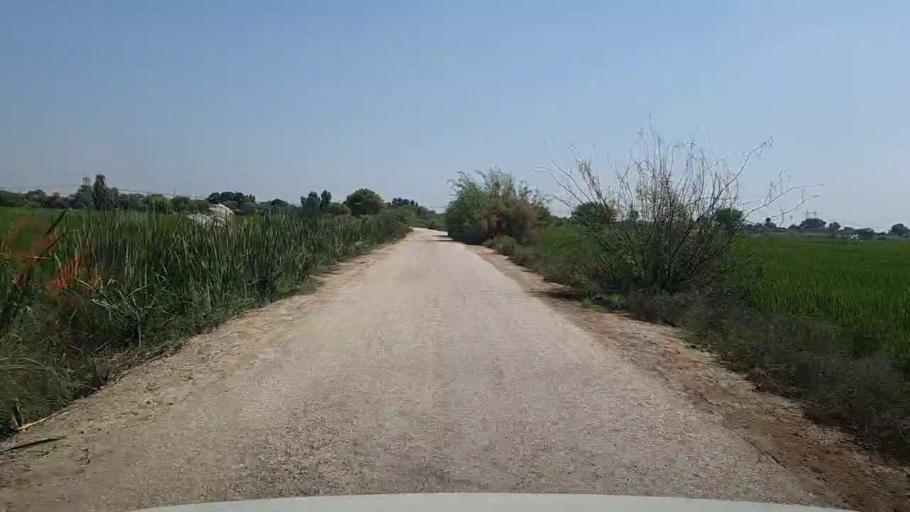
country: PK
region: Sindh
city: Kandhkot
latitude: 28.2916
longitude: 69.3516
